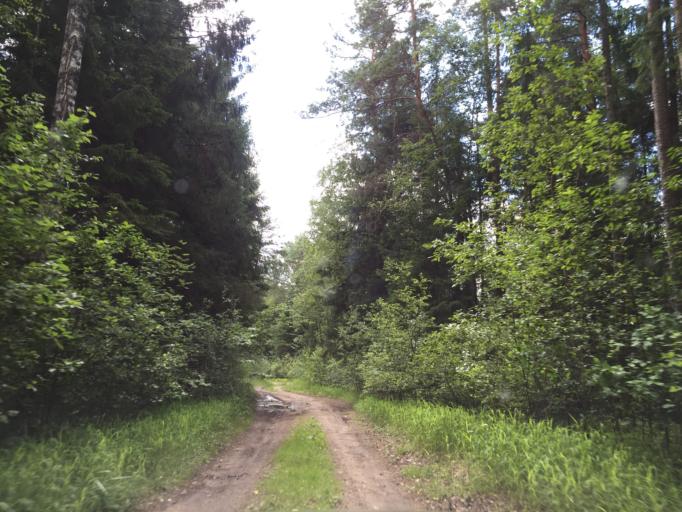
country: LV
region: Ropazu
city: Ropazi
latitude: 56.8994
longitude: 24.7156
